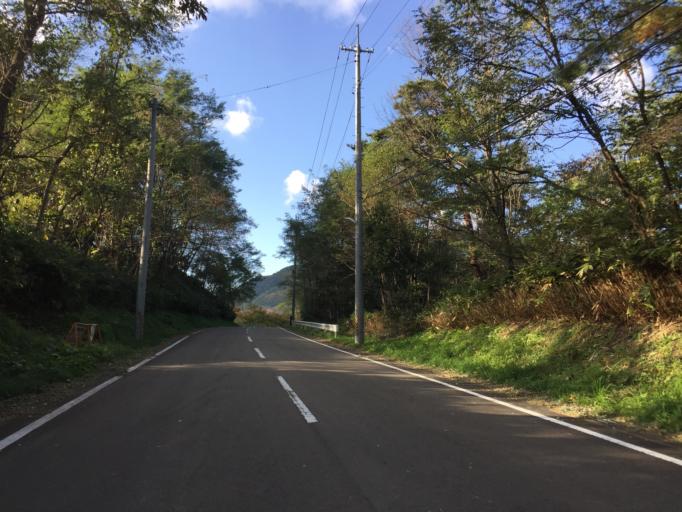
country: JP
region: Fukushima
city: Fukushima-shi
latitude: 37.8379
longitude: 140.4361
